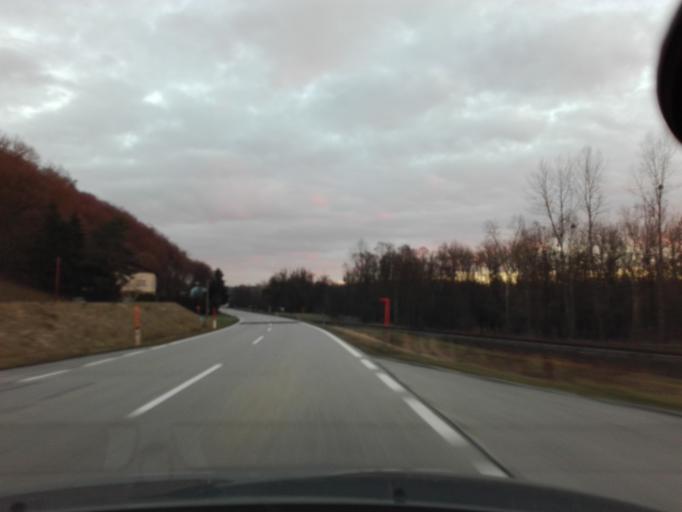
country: AT
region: Upper Austria
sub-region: Politischer Bezirk Perg
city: Bad Kreuzen
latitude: 48.1976
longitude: 14.8113
